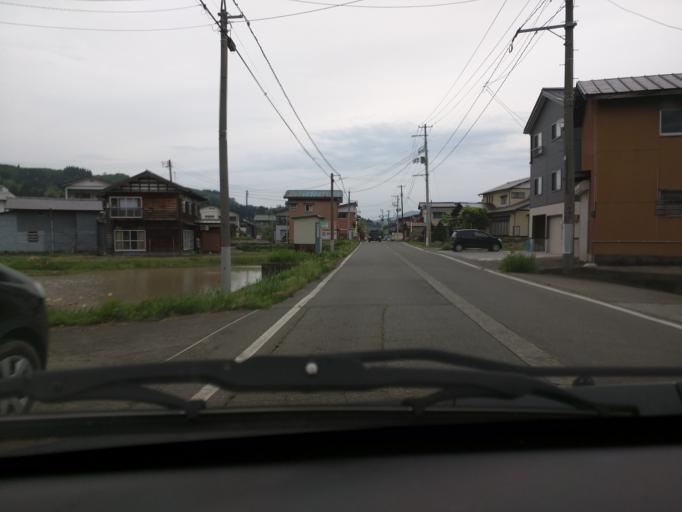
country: JP
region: Niigata
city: Muikamachi
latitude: 37.2130
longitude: 138.9521
